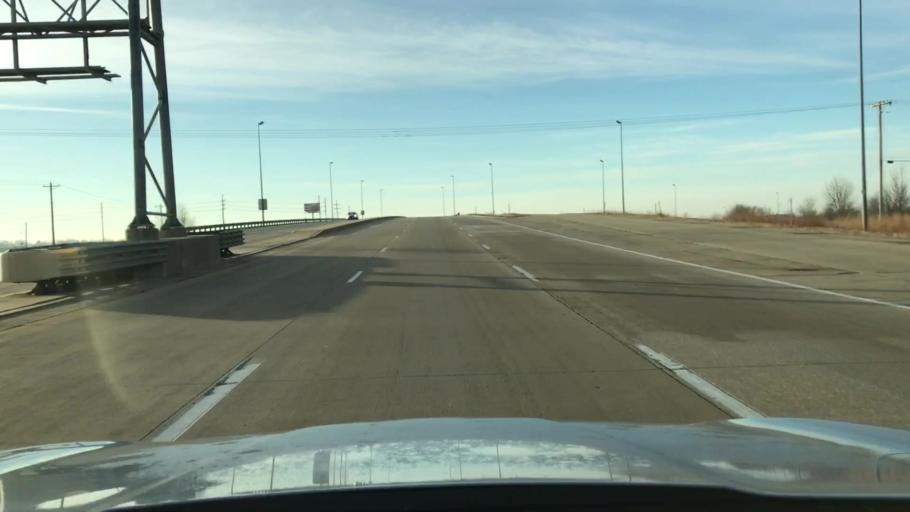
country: US
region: Illinois
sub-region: McLean County
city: Normal
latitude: 40.5329
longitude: -88.9515
